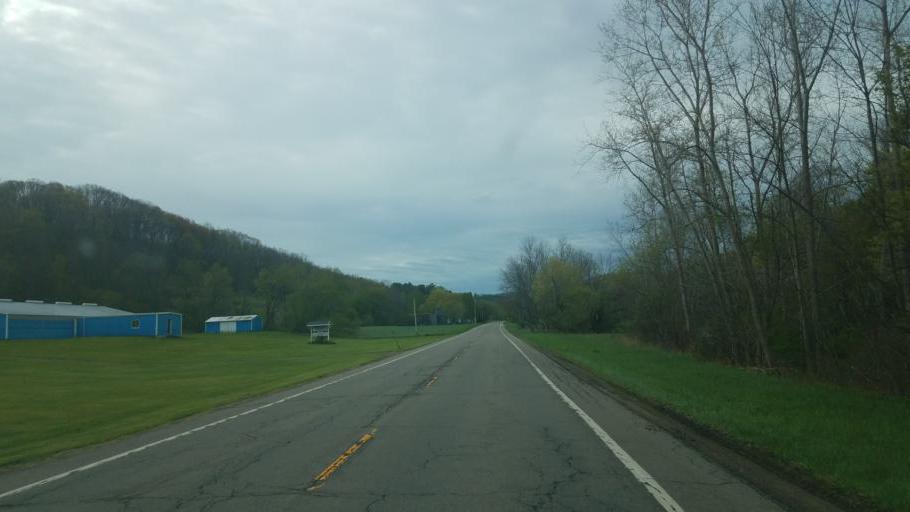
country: US
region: New York
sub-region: Steuben County
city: Canisteo
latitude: 42.2093
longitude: -77.5634
